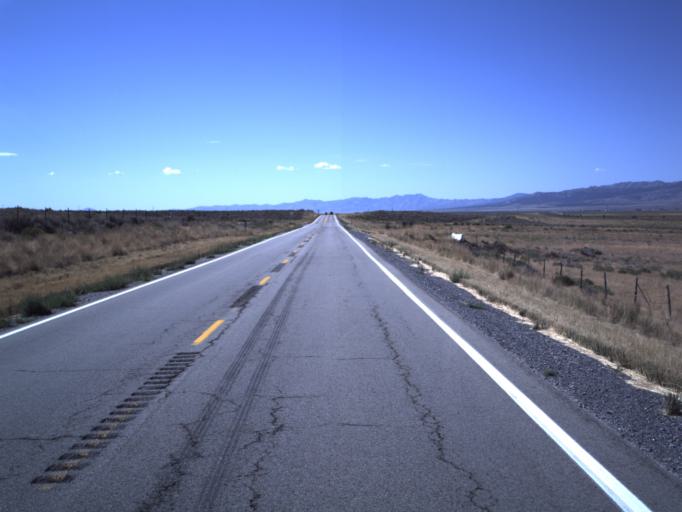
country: US
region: Utah
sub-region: Tooele County
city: Tooele
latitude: 40.4169
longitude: -112.3828
